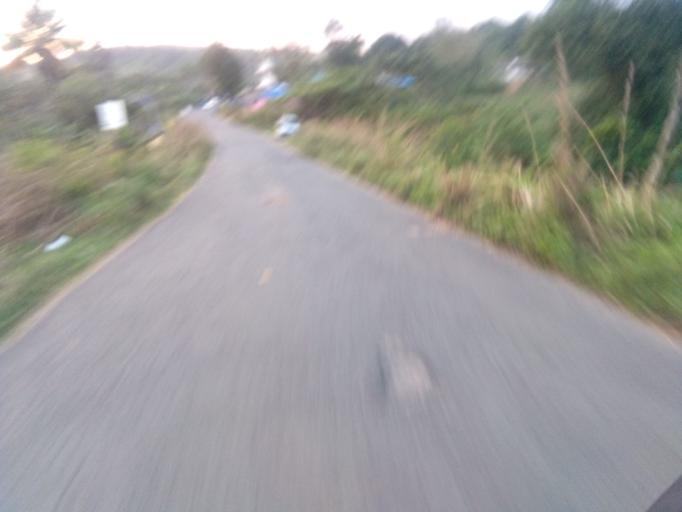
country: IN
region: Kerala
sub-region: Idukki
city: Idukki
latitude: 9.9747
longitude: 76.8853
